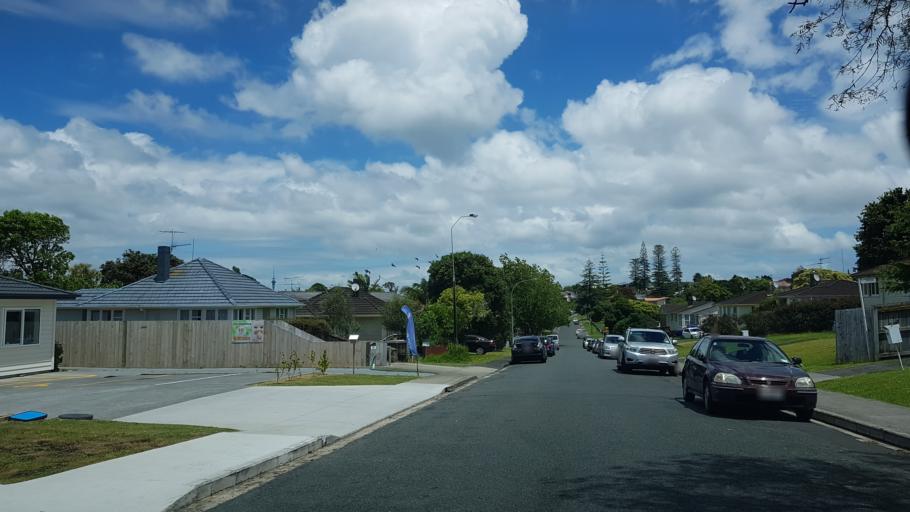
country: NZ
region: Auckland
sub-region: Auckland
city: North Shore
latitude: -36.7983
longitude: 174.7434
